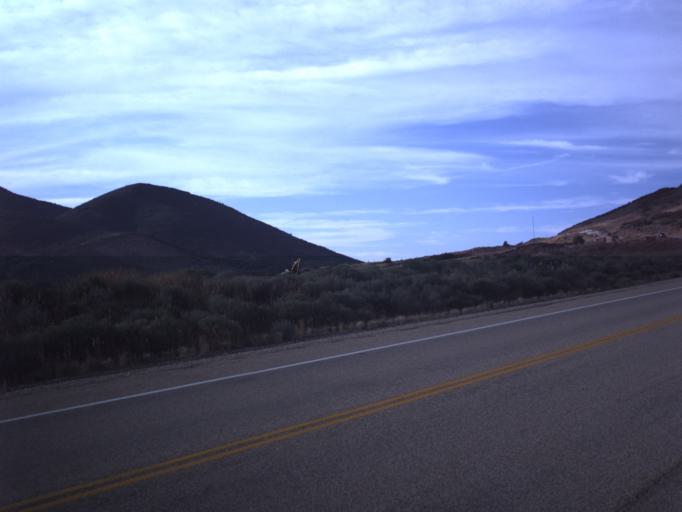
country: US
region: Utah
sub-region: Wasatch County
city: Heber
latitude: 40.5777
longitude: -111.4202
